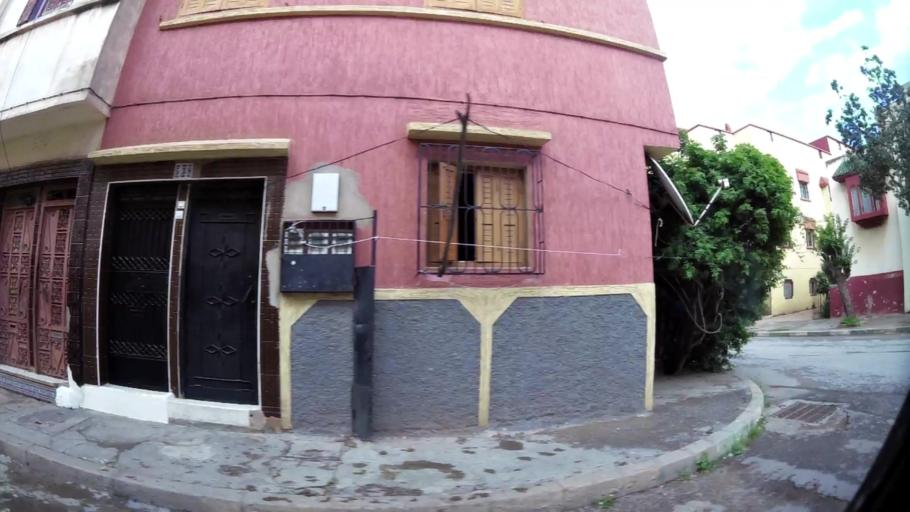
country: MA
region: Grand Casablanca
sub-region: Mohammedia
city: Mohammedia
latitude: 33.6797
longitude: -7.3769
